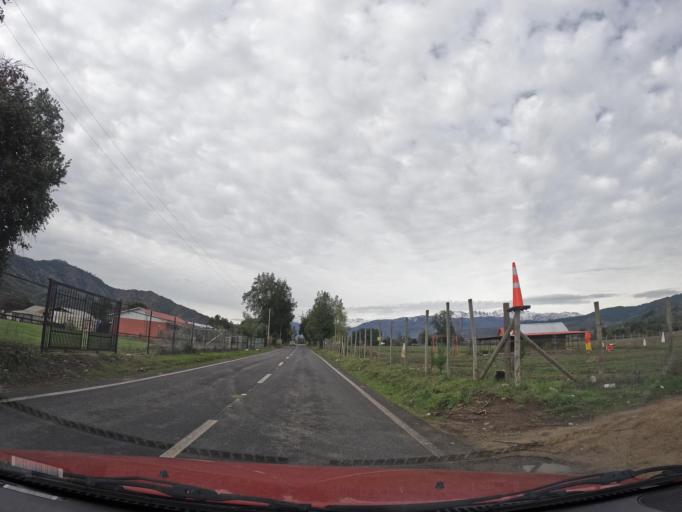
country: CL
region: Maule
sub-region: Provincia de Linares
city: Linares
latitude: -35.9240
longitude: -71.4134
